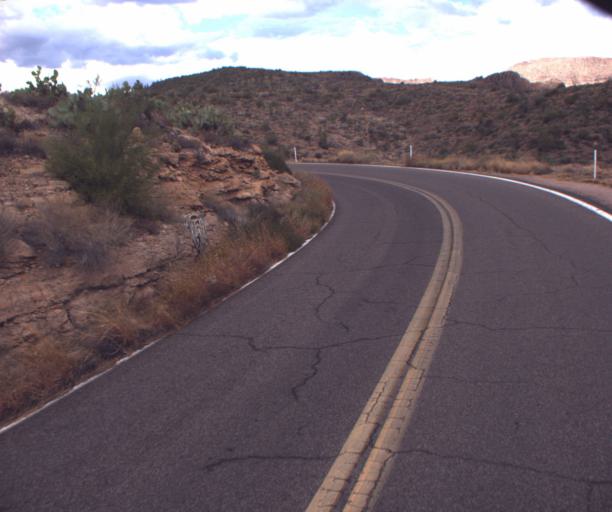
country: US
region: Arizona
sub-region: Pinal County
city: Gold Camp
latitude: 33.5420
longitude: -111.3295
